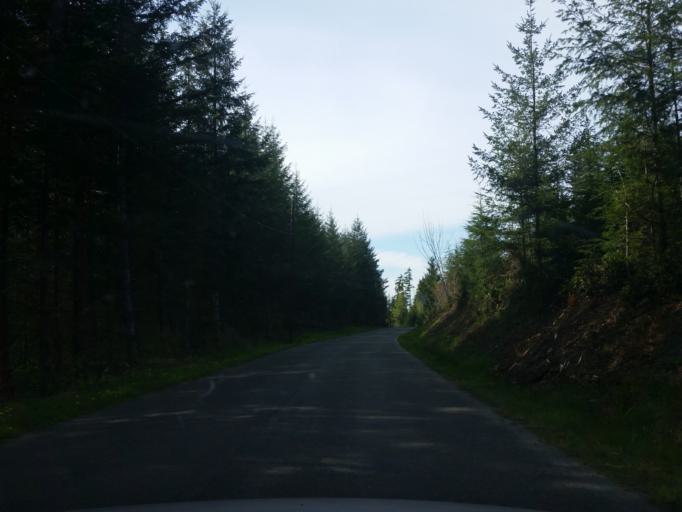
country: US
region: Washington
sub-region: Snohomish County
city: Woods Creek
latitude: 47.9856
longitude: -121.8997
